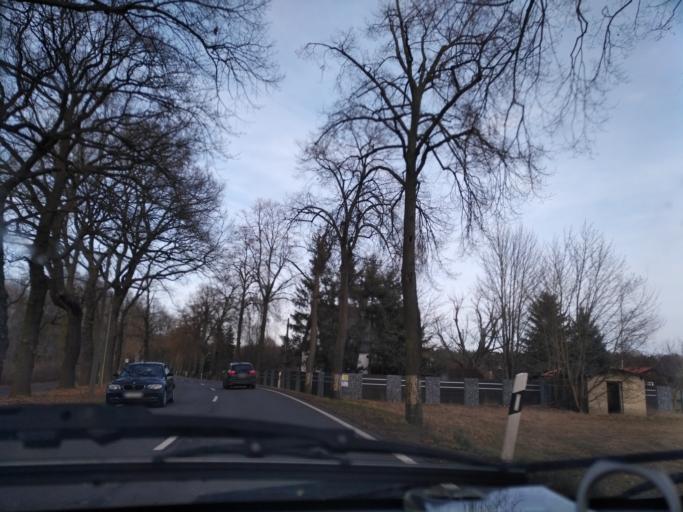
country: DE
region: Brandenburg
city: Luckenwalde
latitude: 52.1069
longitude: 13.1935
